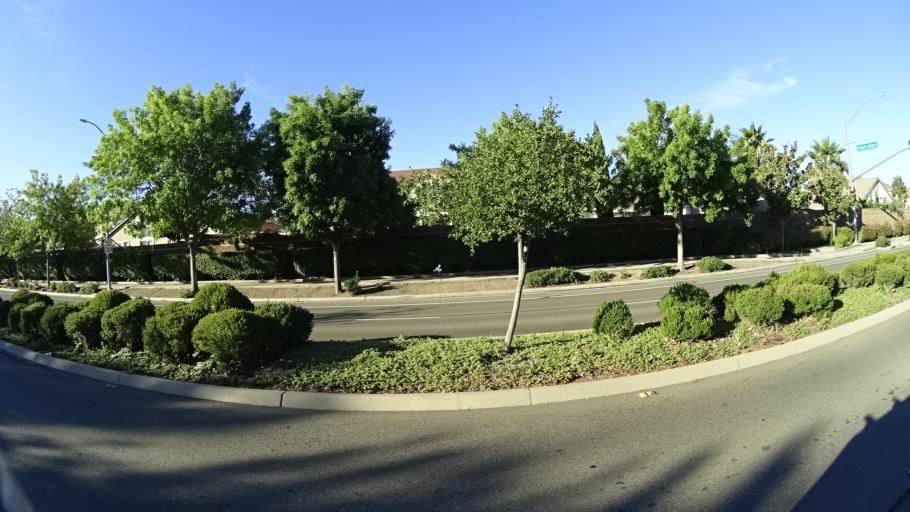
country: US
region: California
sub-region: Sacramento County
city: Laguna
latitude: 38.4472
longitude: -121.3937
